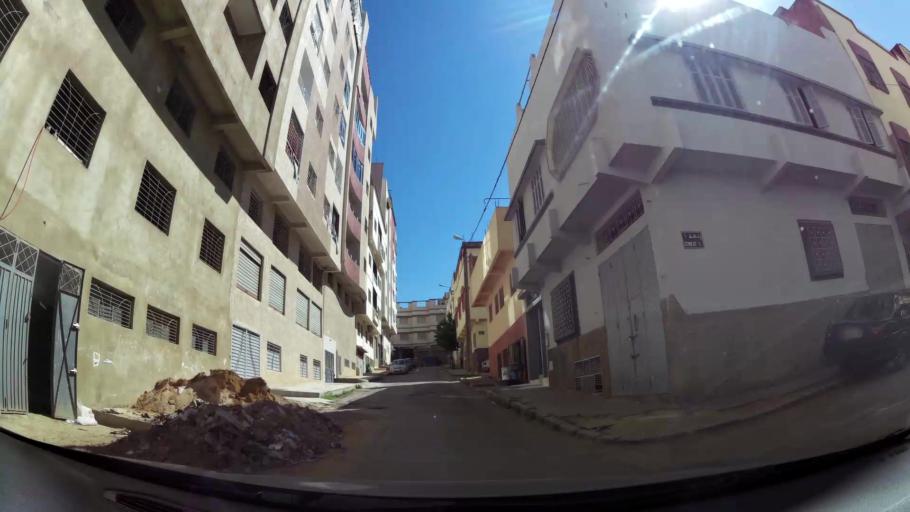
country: MA
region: Meknes-Tafilalet
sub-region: Meknes
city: Meknes
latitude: 33.8821
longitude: -5.5725
